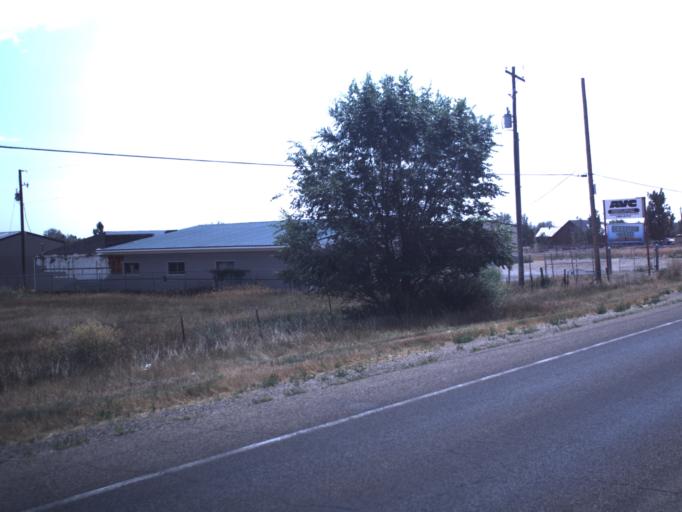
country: US
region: Utah
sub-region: Uintah County
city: Vernal
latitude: 40.4800
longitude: -109.5290
